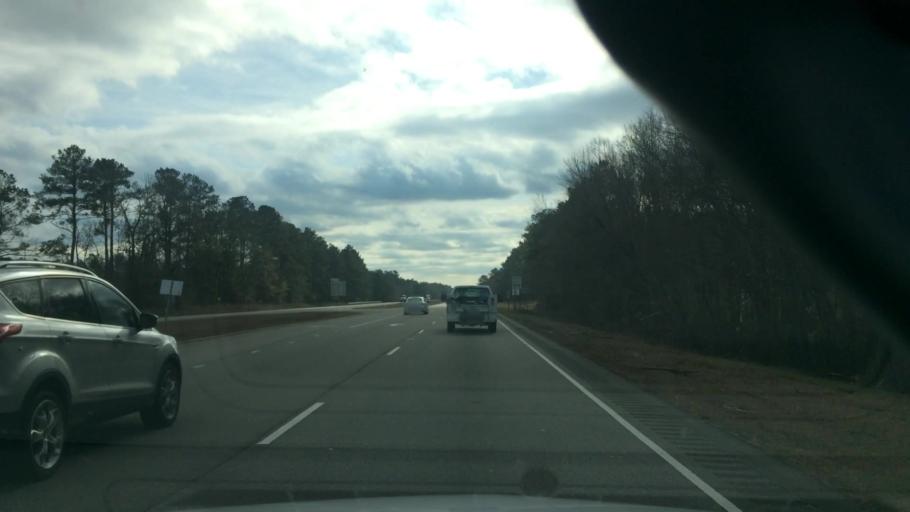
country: US
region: North Carolina
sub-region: Brunswick County
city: Leland
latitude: 34.1710
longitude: -78.0881
